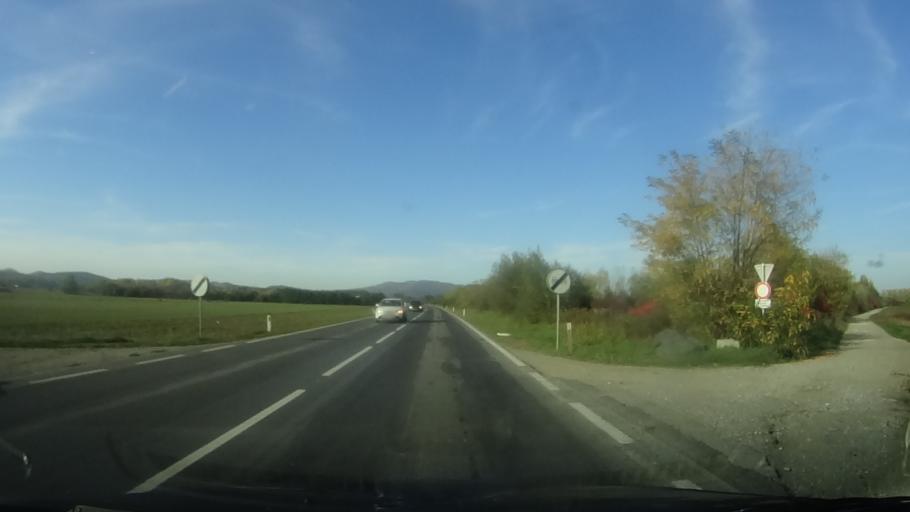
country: AT
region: Styria
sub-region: Politischer Bezirk Leibnitz
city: Kaindorf an der Sulm
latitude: 46.8147
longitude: 15.5262
